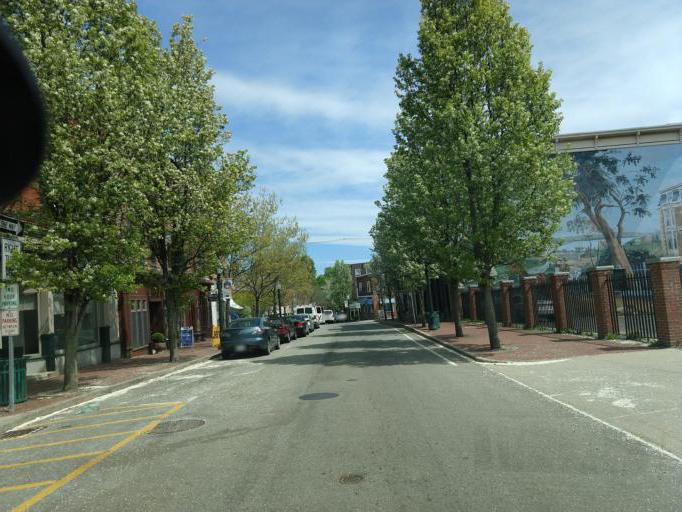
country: US
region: Massachusetts
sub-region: Essex County
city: Amesbury
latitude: 42.8566
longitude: -70.9311
